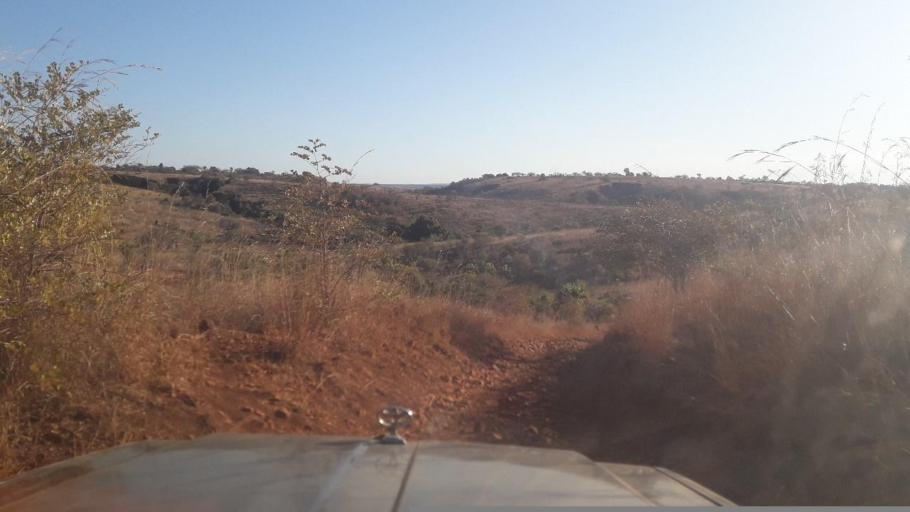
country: MG
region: Boeny
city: Sitampiky
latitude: -16.4922
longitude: 45.6077
